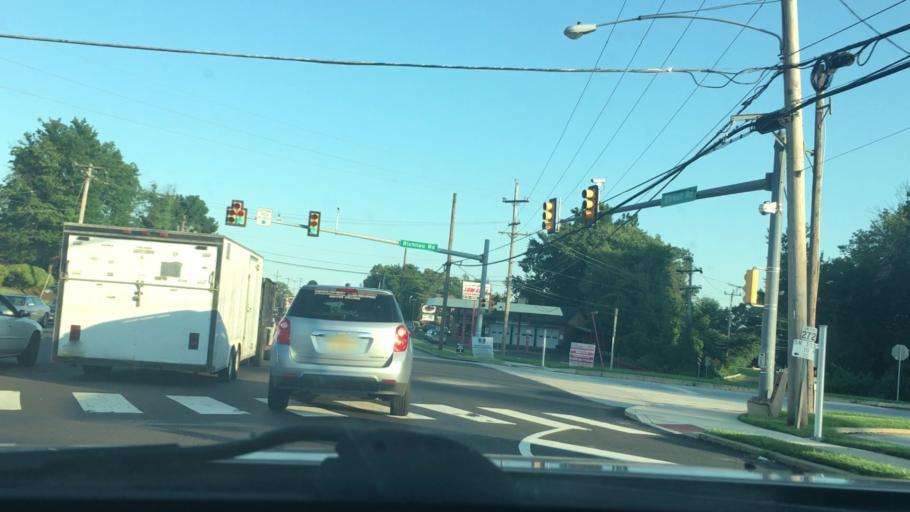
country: US
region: Pennsylvania
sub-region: Bucks County
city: Trevose
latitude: 40.1210
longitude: -74.9618
